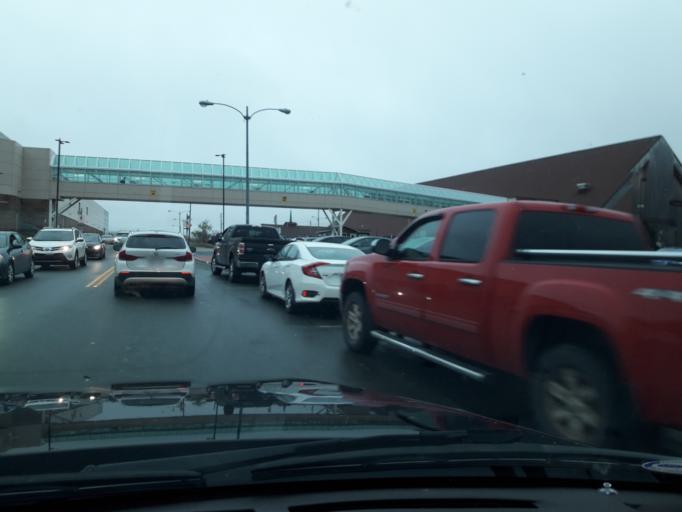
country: CA
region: Newfoundland and Labrador
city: St. John's
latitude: 47.5704
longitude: -52.7364
